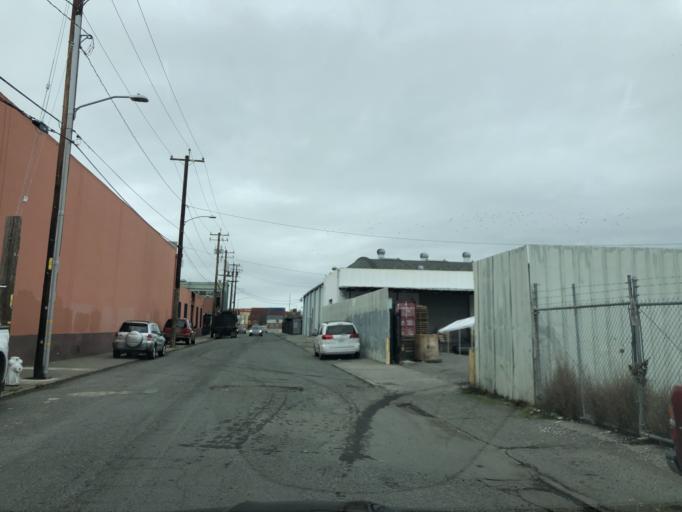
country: US
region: California
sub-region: Alameda County
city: San Leandro
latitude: 37.7392
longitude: -122.1776
